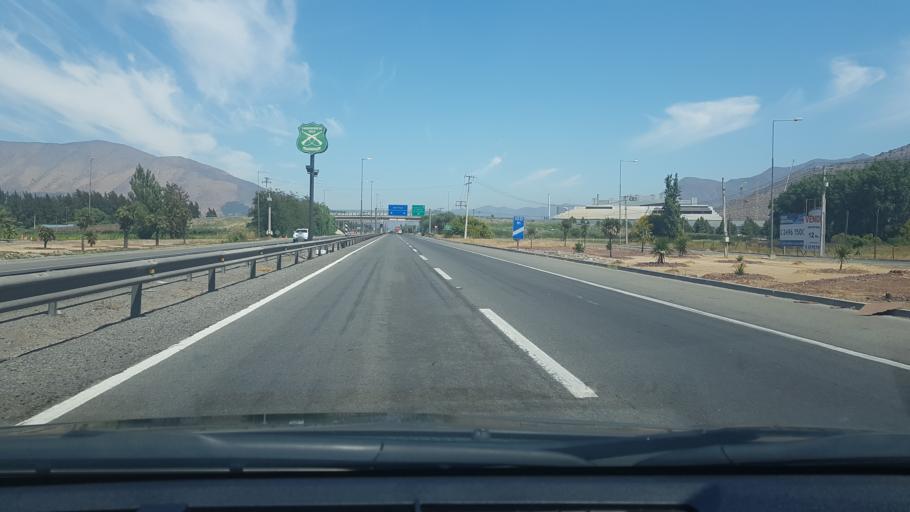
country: CL
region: Valparaiso
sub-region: Provincia de San Felipe
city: Llaillay
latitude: -32.8514
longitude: -70.9398
